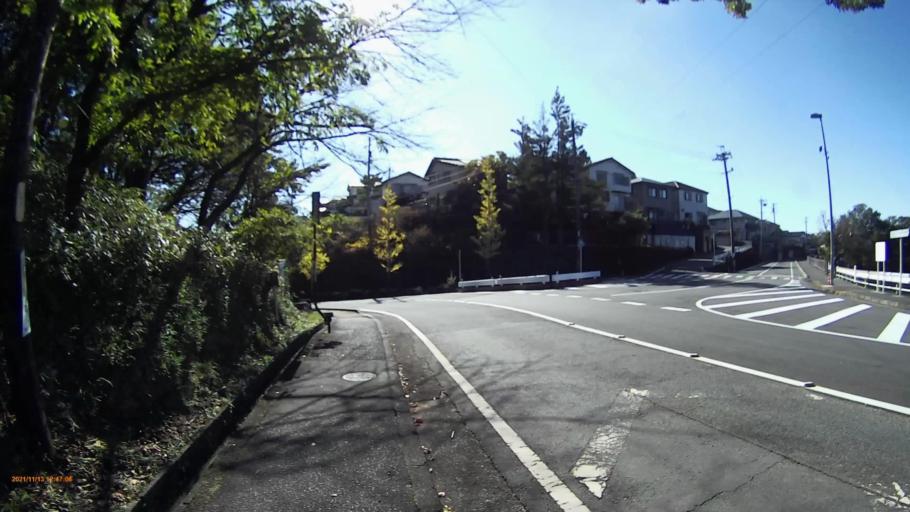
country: JP
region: Gifu
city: Inuyama
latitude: 35.4089
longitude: 136.9481
